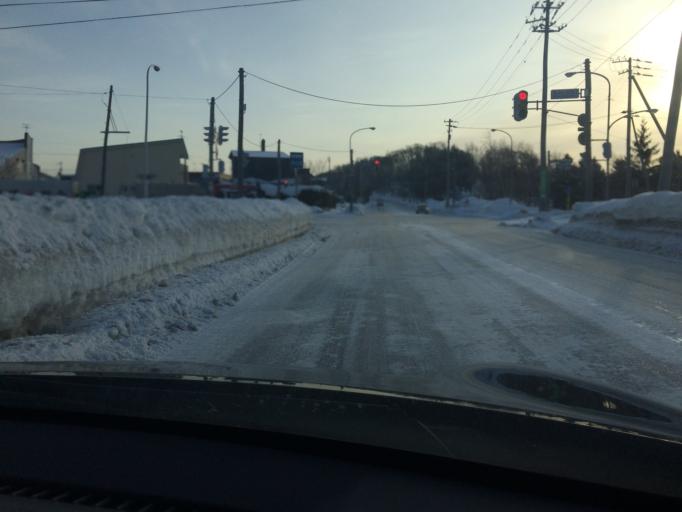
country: JP
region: Hokkaido
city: Kitahiroshima
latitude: 43.0239
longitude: 141.4865
